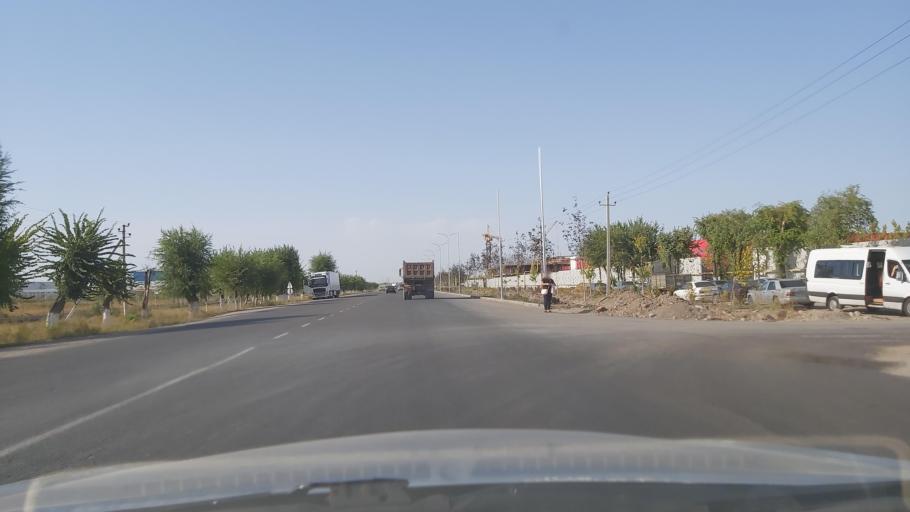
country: KZ
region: Almaty Oblysy
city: Energeticheskiy
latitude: 43.4570
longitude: 77.0340
